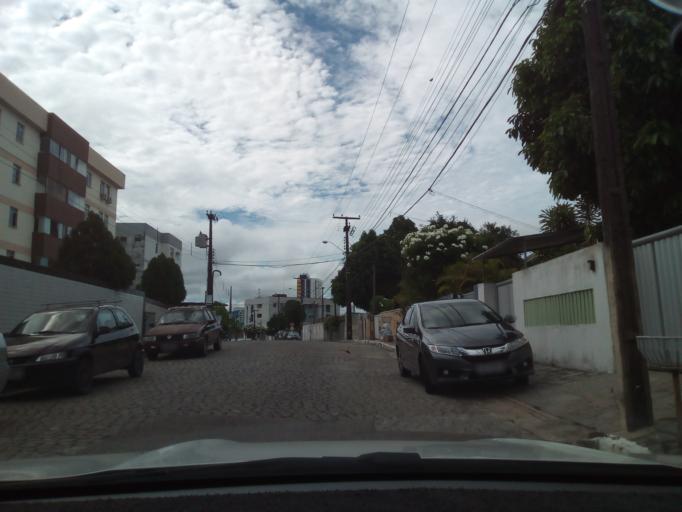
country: BR
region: Paraiba
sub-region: Joao Pessoa
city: Joao Pessoa
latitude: -7.1270
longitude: -34.8566
